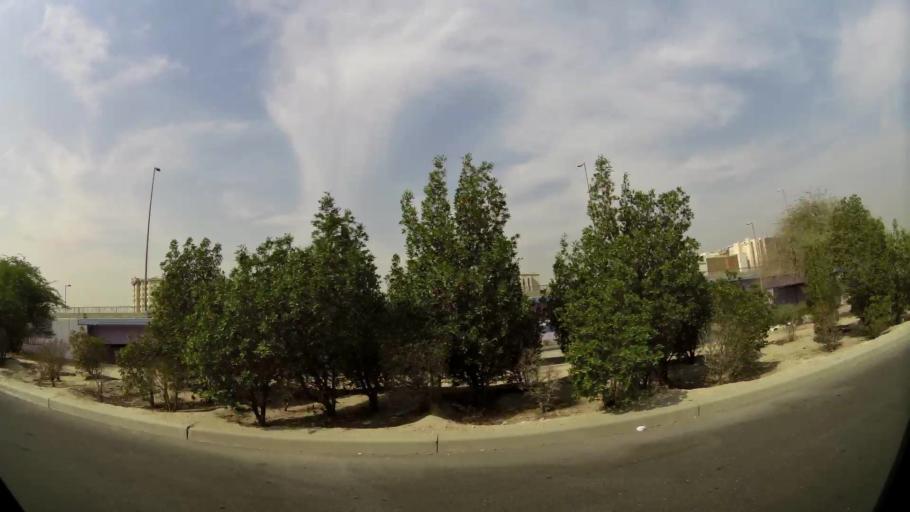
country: KW
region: Al Farwaniyah
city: Janub as Surrah
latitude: 29.2688
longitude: 47.9707
